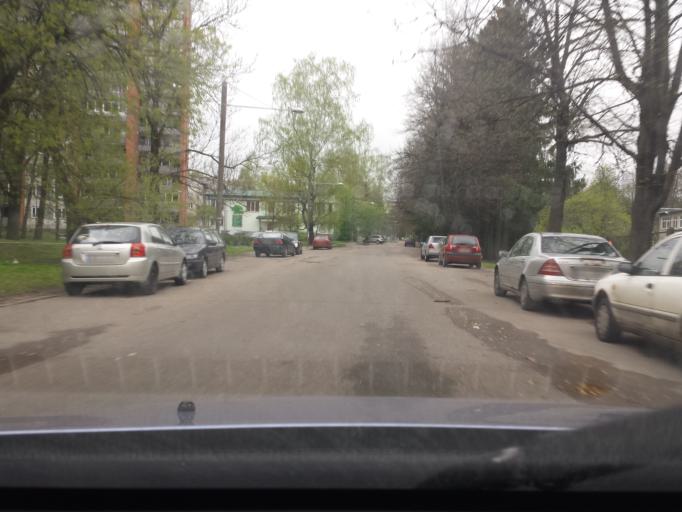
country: LV
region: Marupe
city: Marupe
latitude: 56.9607
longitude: 24.0301
